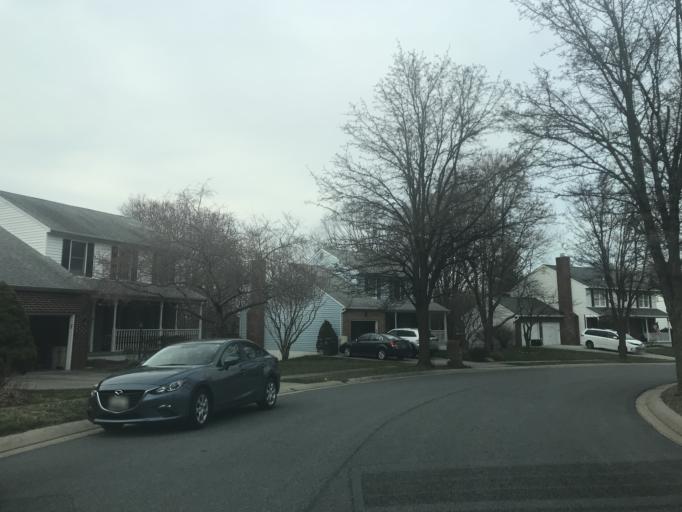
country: US
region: Maryland
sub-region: Harford County
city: South Bel Air
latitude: 39.5360
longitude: -76.3248
